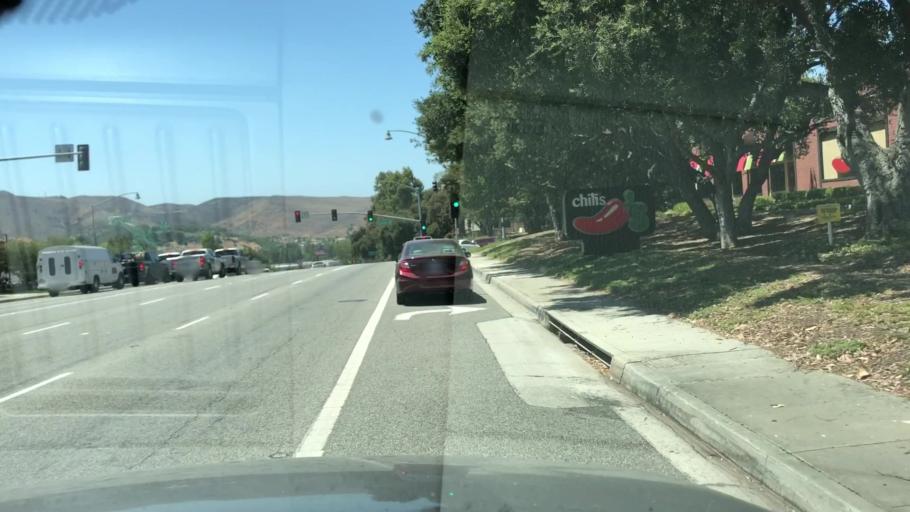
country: US
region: California
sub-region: Ventura County
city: Simi Valley
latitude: 34.2824
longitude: -118.7946
